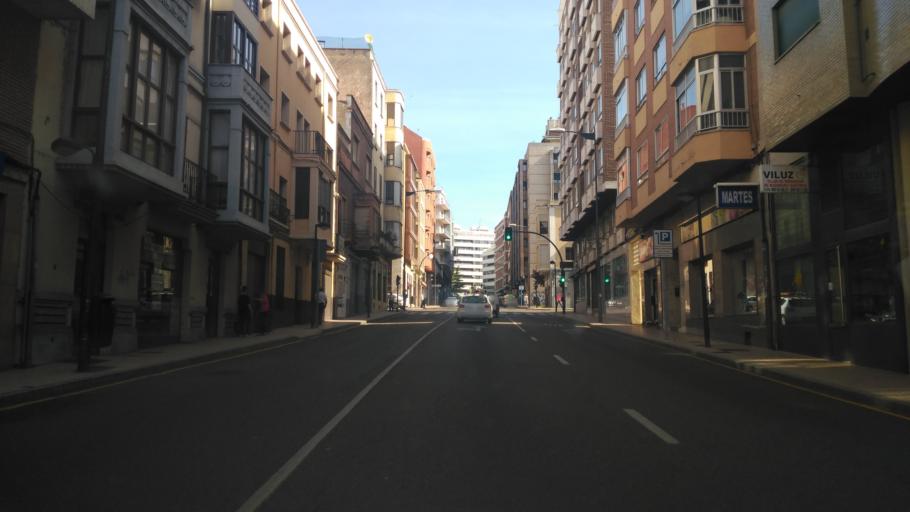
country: ES
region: Castille and Leon
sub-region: Provincia de Zamora
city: Zamora
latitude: 41.5038
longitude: -5.7399
